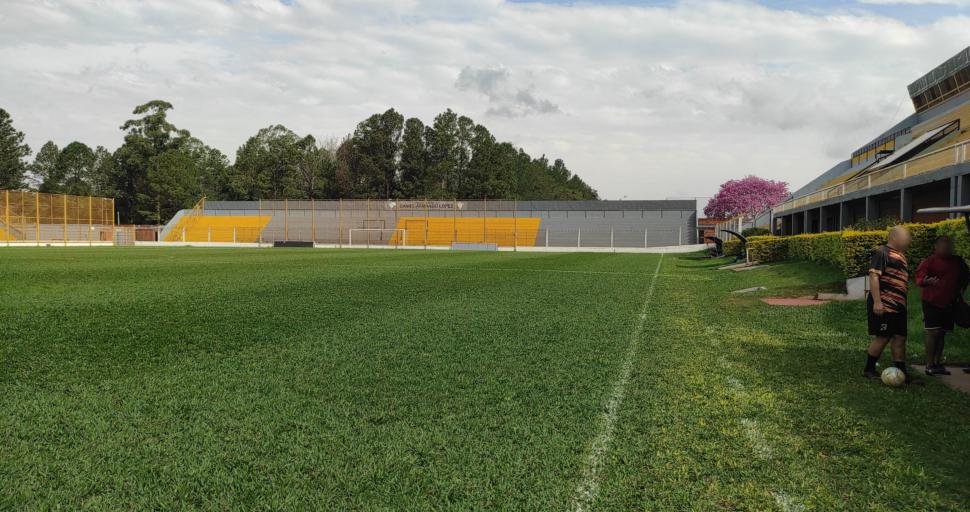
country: AR
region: Misiones
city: Garupa
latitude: -27.4983
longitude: -55.8525
